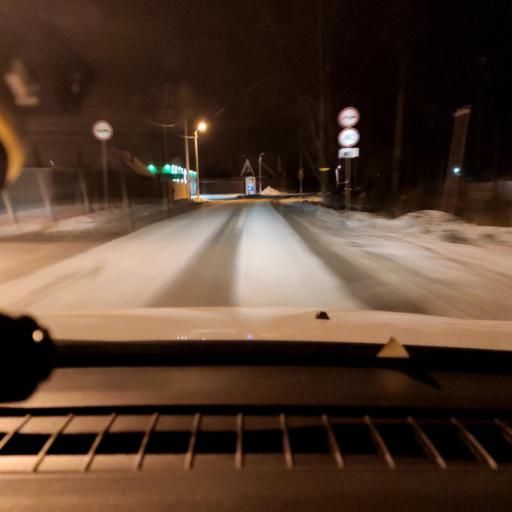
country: RU
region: Samara
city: Novokuybyshevsk
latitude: 53.1450
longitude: 49.9832
